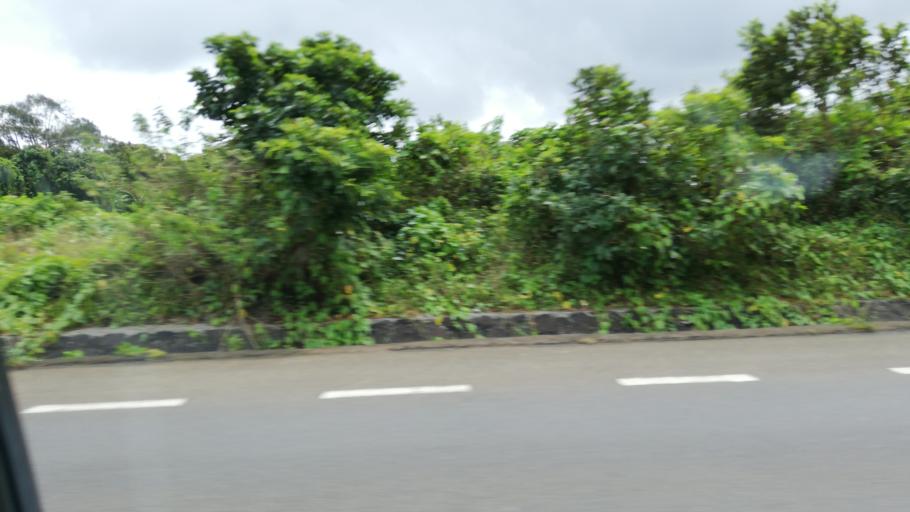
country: MU
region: Plaines Wilhems
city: Curepipe
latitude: -20.2954
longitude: 57.5429
